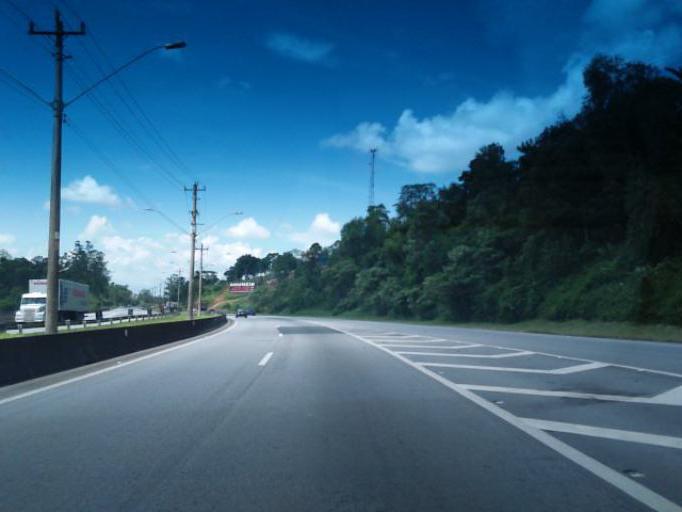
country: BR
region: Sao Paulo
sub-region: Sao Lourenco Da Serra
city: Sao Lourenco da Serra
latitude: -23.8597
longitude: -46.9457
